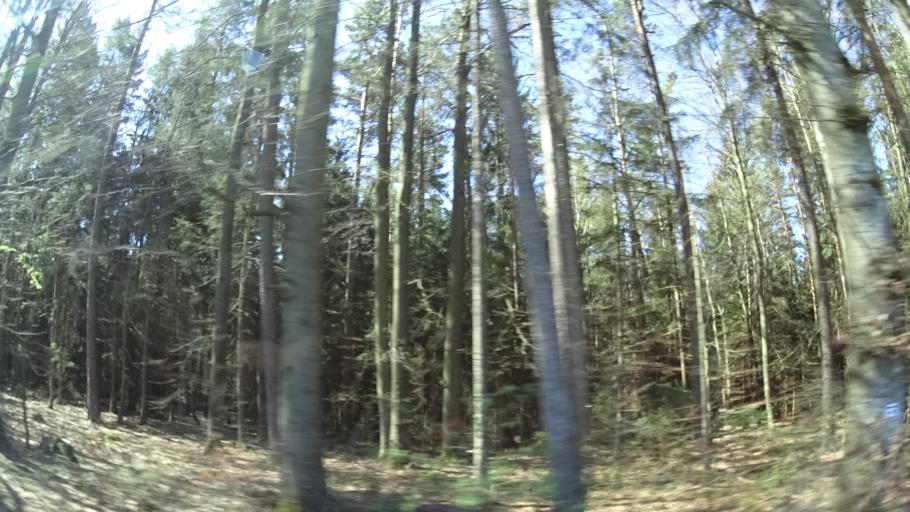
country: DE
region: Bavaria
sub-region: Regierungsbezirk Mittelfranken
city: Alfeld
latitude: 49.4166
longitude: 11.5648
